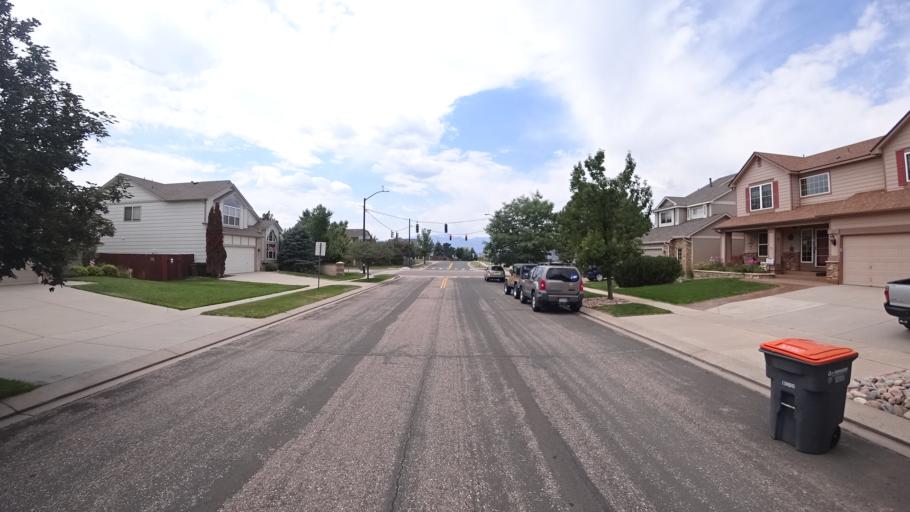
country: US
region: Colorado
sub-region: El Paso County
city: Black Forest
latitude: 38.9646
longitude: -104.7727
